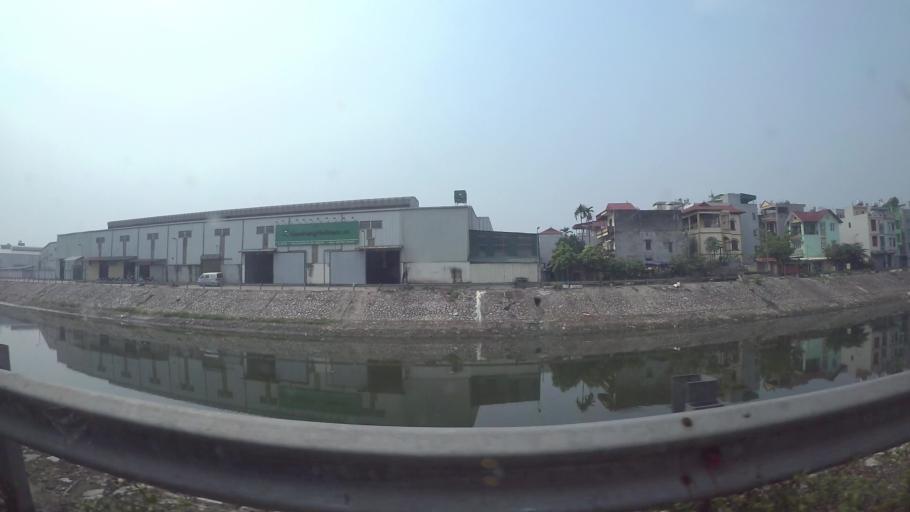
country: VN
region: Ha Noi
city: Van Dien
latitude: 20.9602
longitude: 105.8160
